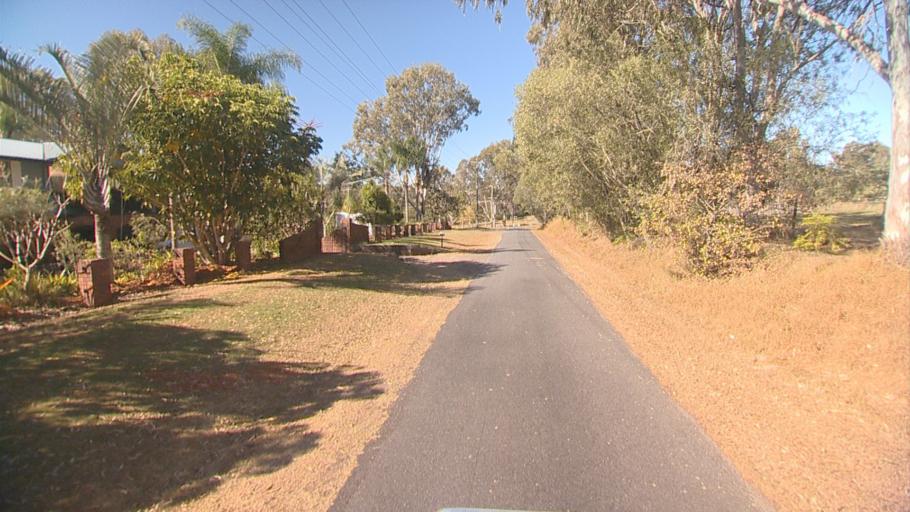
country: AU
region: Queensland
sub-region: Logan
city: North Maclean
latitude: -27.7766
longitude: 153.0234
